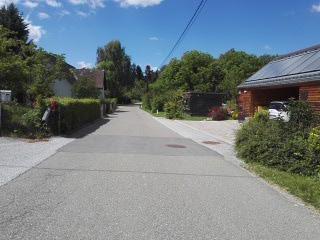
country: AT
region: Styria
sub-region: Graz Stadt
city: Mariatrost
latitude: 47.0814
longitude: 15.5345
